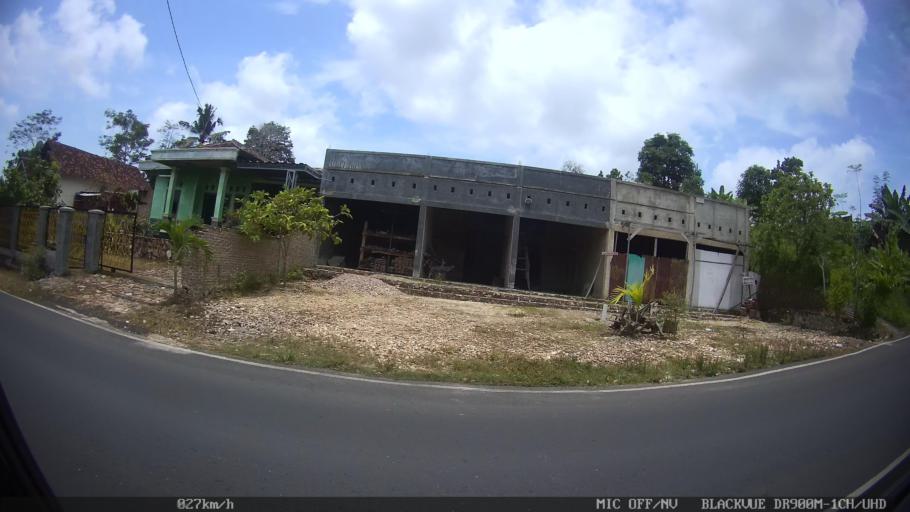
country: ID
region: Lampung
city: Bandarlampung
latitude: -5.4137
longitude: 105.2339
